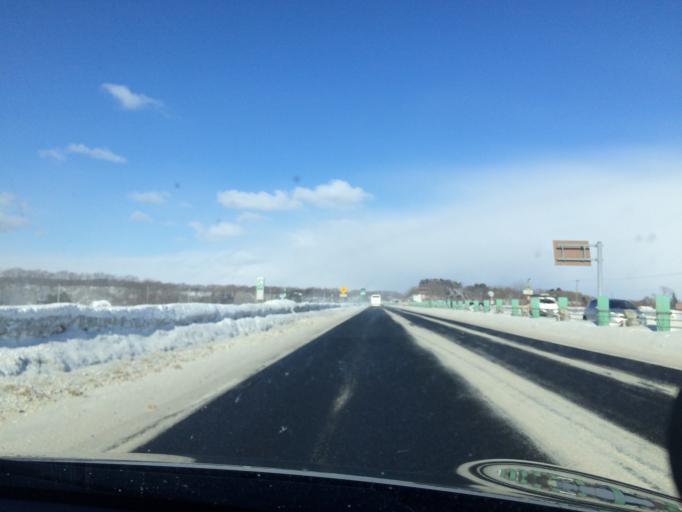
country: JP
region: Hokkaido
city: Kitahiroshima
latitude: 42.8742
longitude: 141.5532
